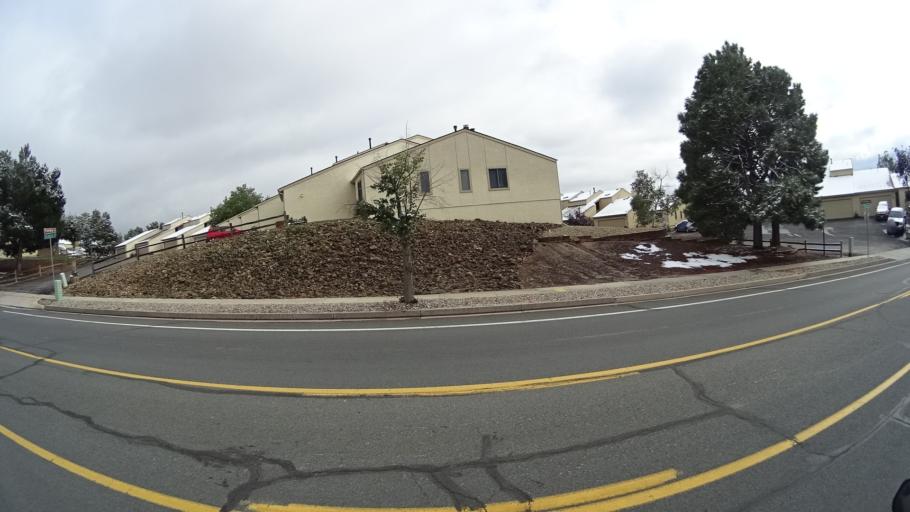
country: US
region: Colorado
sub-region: El Paso County
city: Cimarron Hills
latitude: 38.9159
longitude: -104.7628
